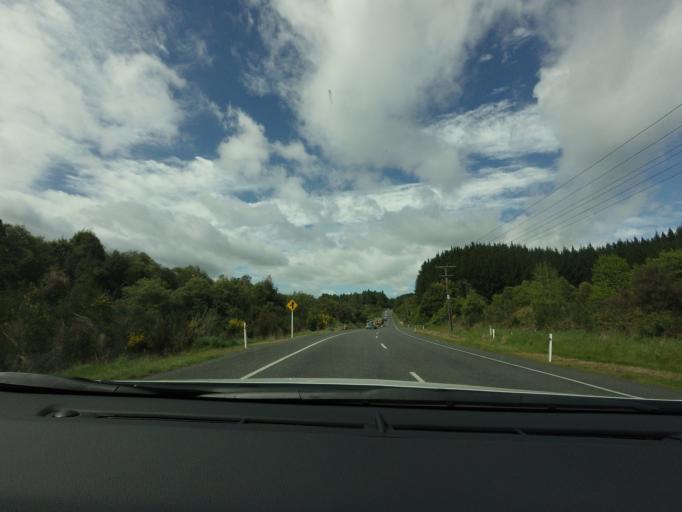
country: NZ
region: Bay of Plenty
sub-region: Rotorua District
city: Rotorua
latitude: -38.3201
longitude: 176.3738
